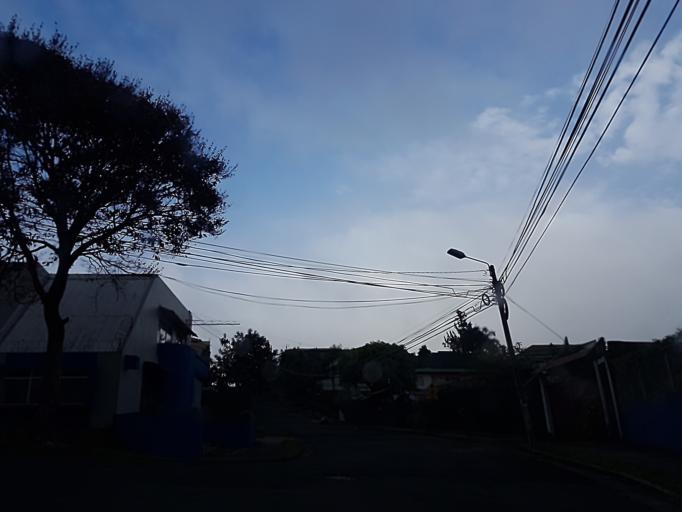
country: CR
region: San Jose
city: San Pedro
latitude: 9.9290
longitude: -84.0509
